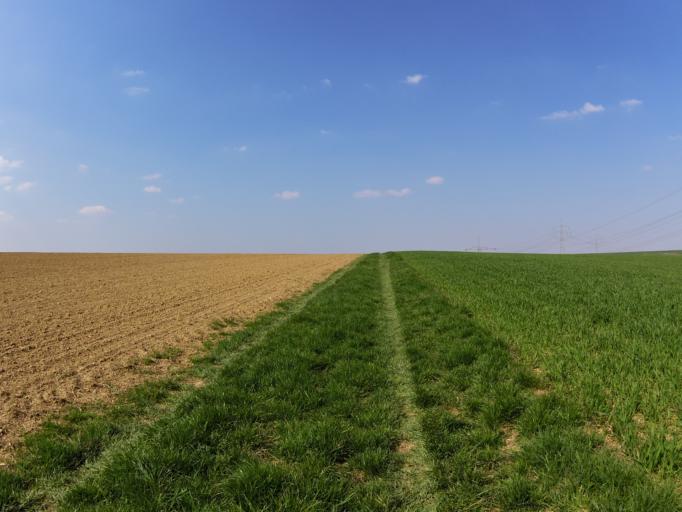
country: DE
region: Bavaria
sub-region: Regierungsbezirk Unterfranken
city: Rottendorf
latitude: 49.7790
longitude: 10.0465
